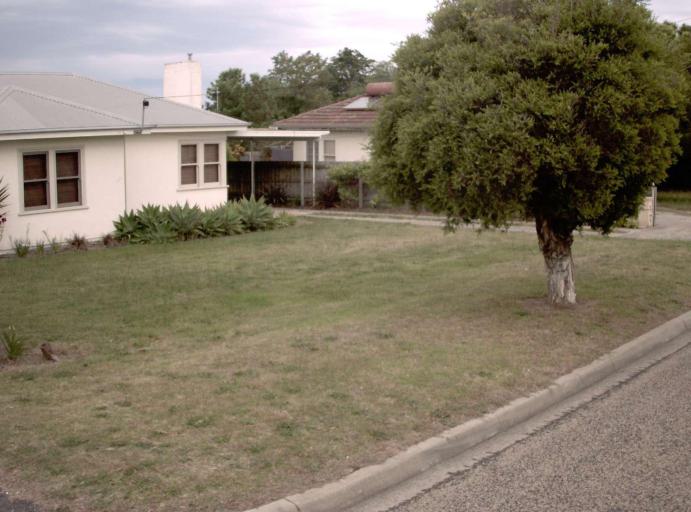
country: AU
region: Victoria
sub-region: East Gippsland
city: Bairnsdale
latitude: -37.9127
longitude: 147.7196
